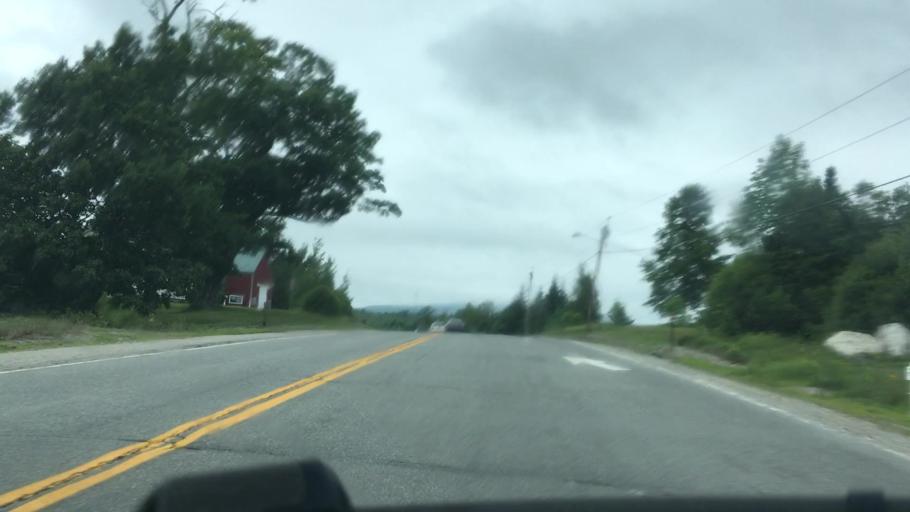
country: US
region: Maine
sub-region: Washington County
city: Cherryfield
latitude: 44.8479
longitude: -68.0621
